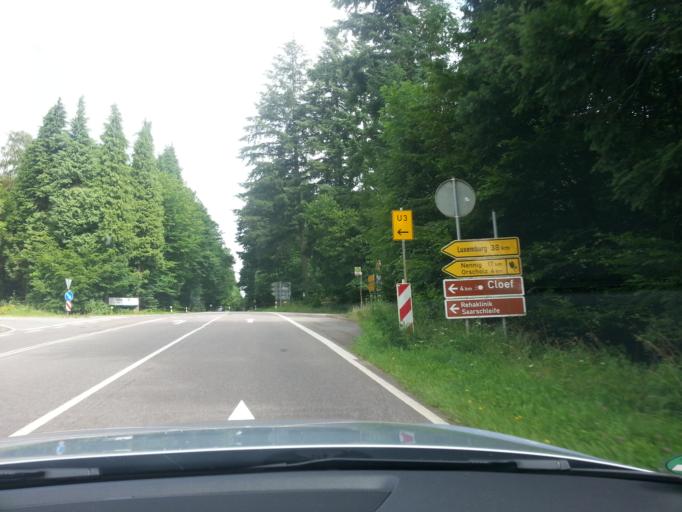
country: DE
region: Saarland
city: Mettlach
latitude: 49.5101
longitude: 6.5692
